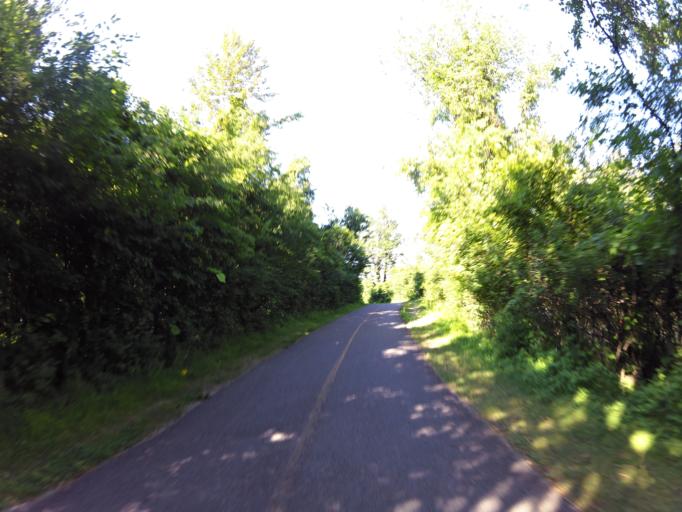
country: CA
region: Quebec
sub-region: Outaouais
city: Gatineau
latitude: 45.4555
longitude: -75.7207
